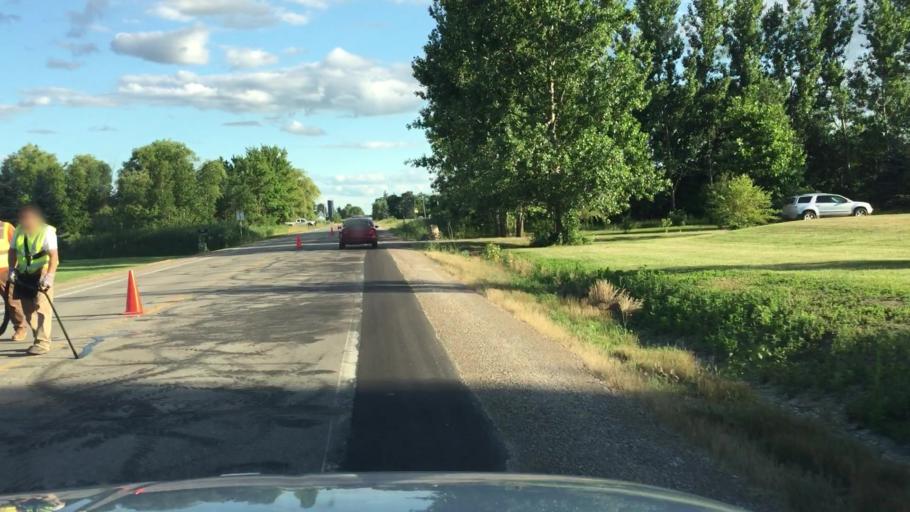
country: US
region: Michigan
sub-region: Saint Clair County
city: Yale
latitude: 43.0991
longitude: -82.7668
